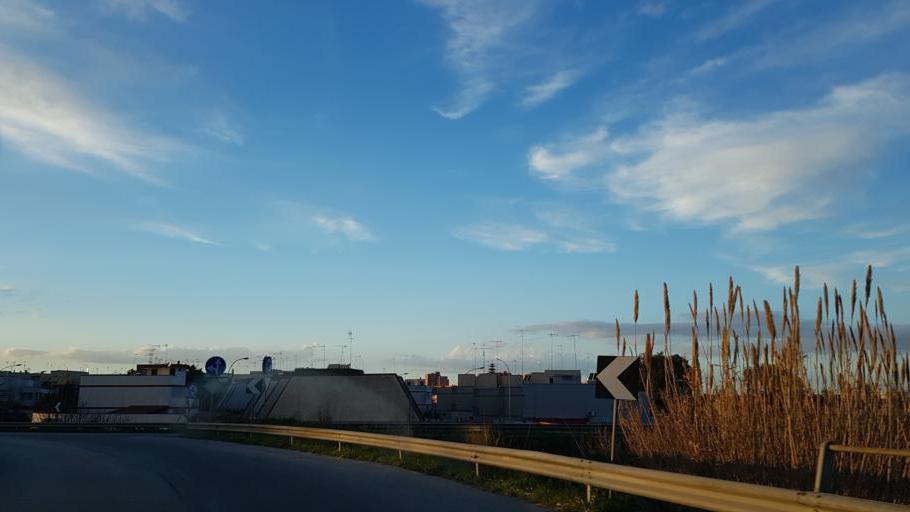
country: IT
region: Apulia
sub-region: Provincia di Brindisi
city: La Rosa
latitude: 40.6257
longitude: 17.9575
